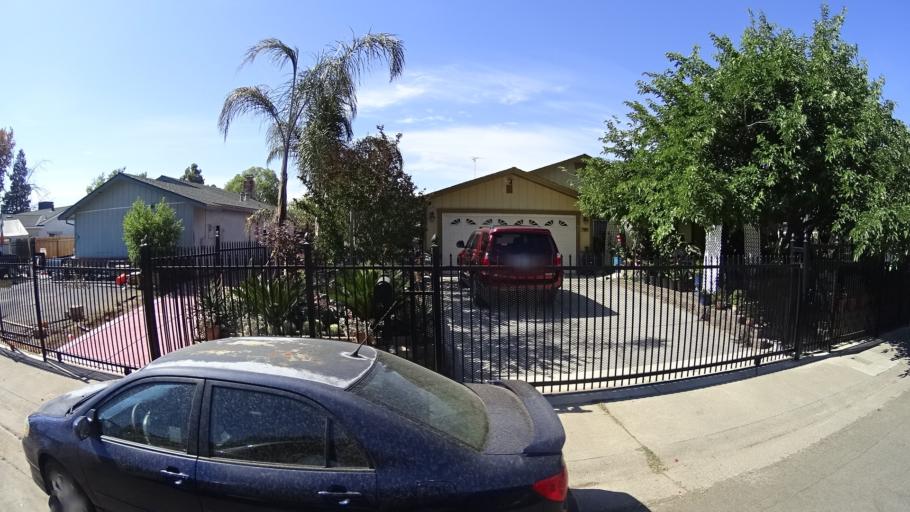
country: US
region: California
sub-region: Sacramento County
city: Florin
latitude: 38.5007
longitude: -121.4145
